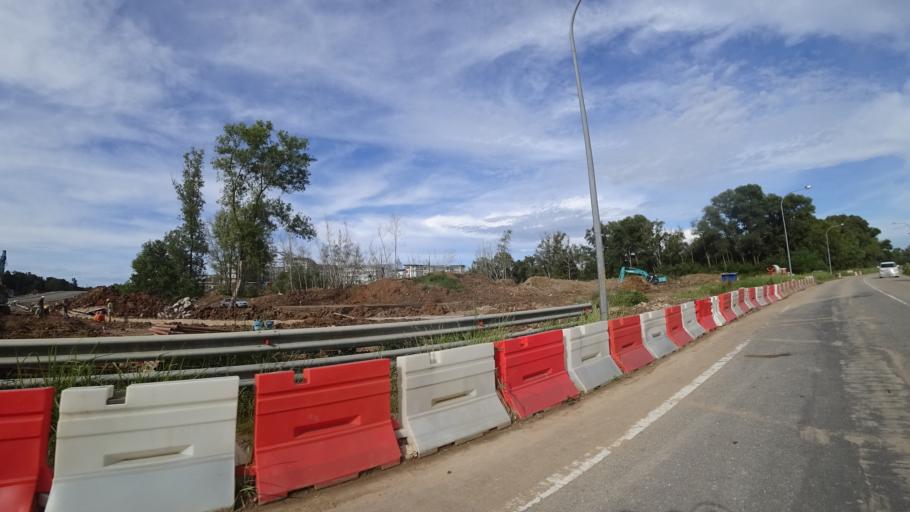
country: BN
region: Brunei and Muara
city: Bandar Seri Begawan
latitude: 4.9539
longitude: 114.9111
